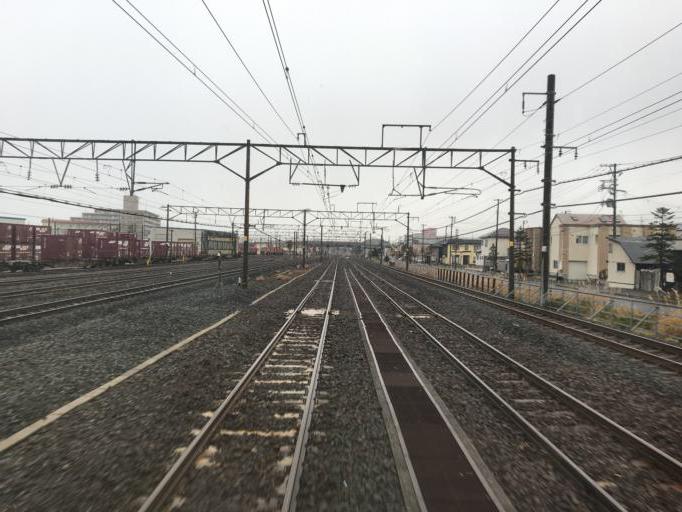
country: JP
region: Aomori
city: Aomori Shi
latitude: 40.8117
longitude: 140.7854
